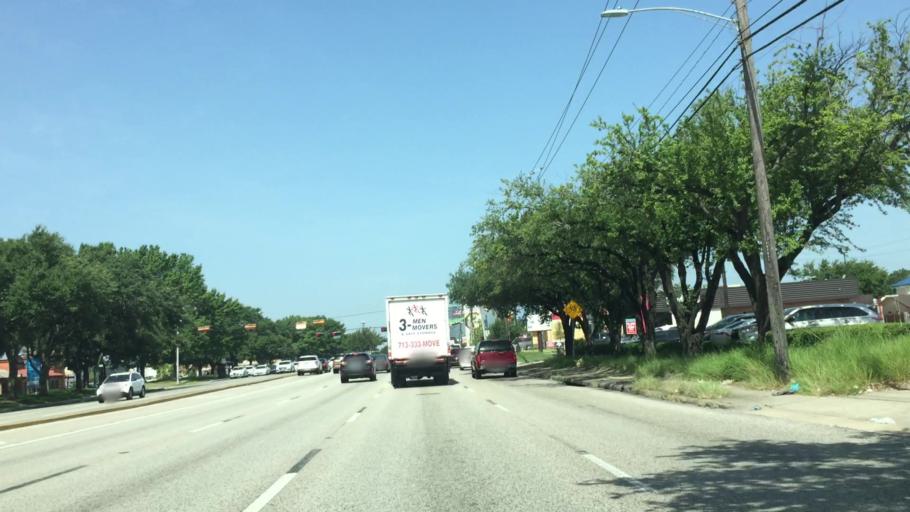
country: US
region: Texas
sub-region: Harris County
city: Bunker Hill Village
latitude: 29.7369
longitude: -95.5658
